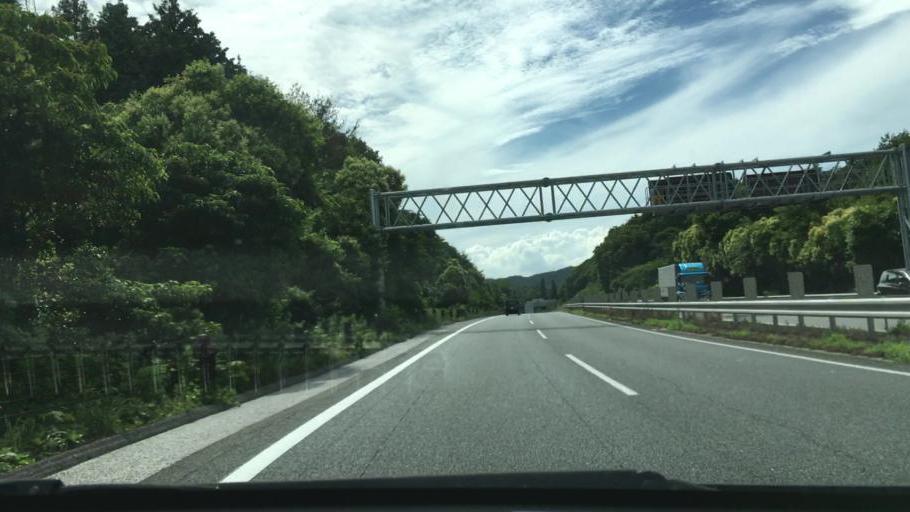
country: JP
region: Yamaguchi
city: Ogori-shimogo
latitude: 34.1259
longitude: 131.3917
